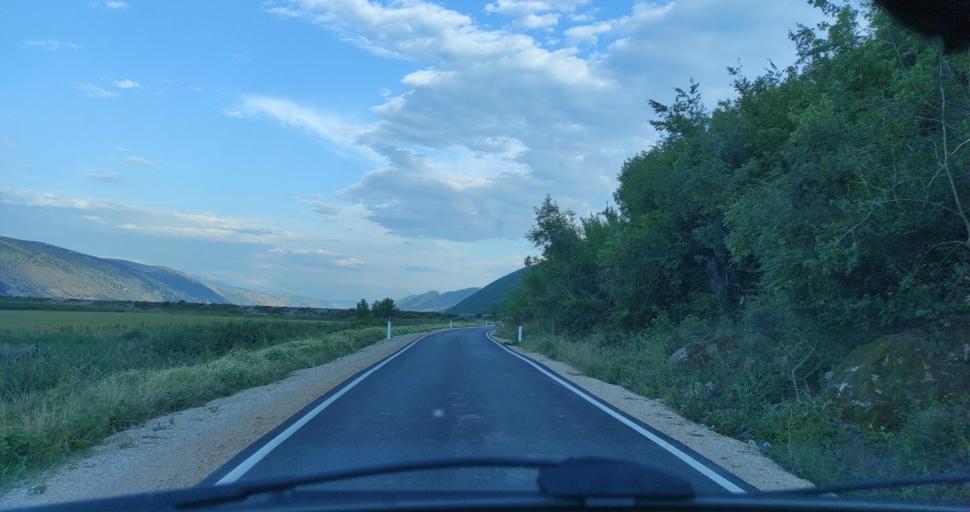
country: AL
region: Shkoder
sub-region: Rrethi i Shkodres
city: Velipoje
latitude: 41.9249
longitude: 19.4500
